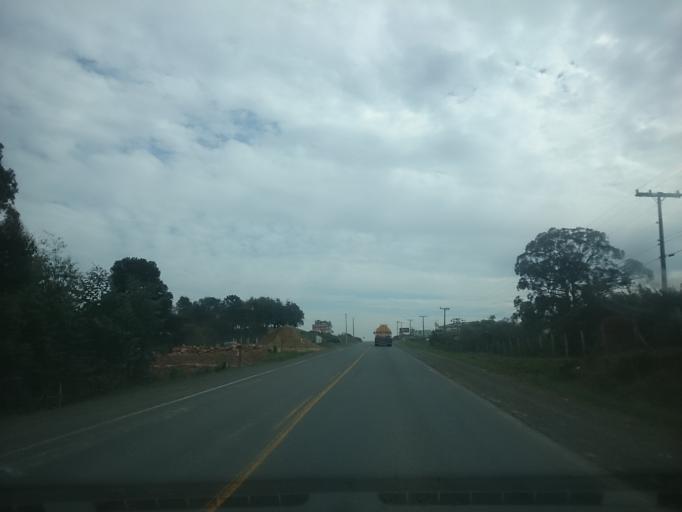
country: BR
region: Santa Catarina
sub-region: Lages
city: Lages
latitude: -27.7732
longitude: -50.3205
